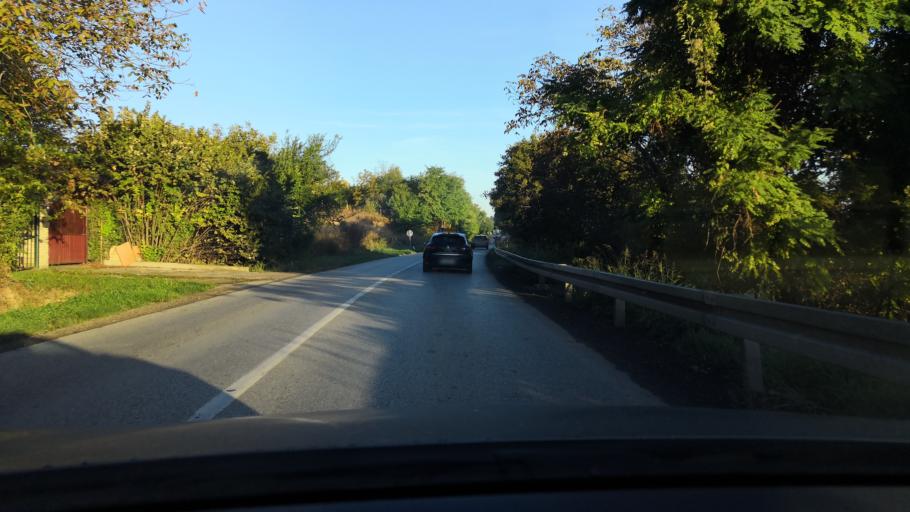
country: RS
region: Autonomna Pokrajina Vojvodina
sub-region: Juznobacki Okrug
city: Petrovaradin
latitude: 45.2206
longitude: 19.9028
